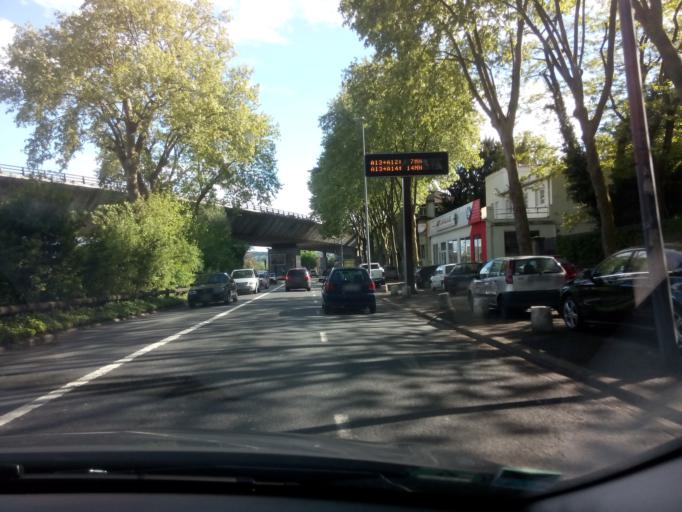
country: FR
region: Ile-de-France
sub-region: Departement des Hauts-de-Seine
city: Saint-Cloud
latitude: 48.8479
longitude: 2.2239
